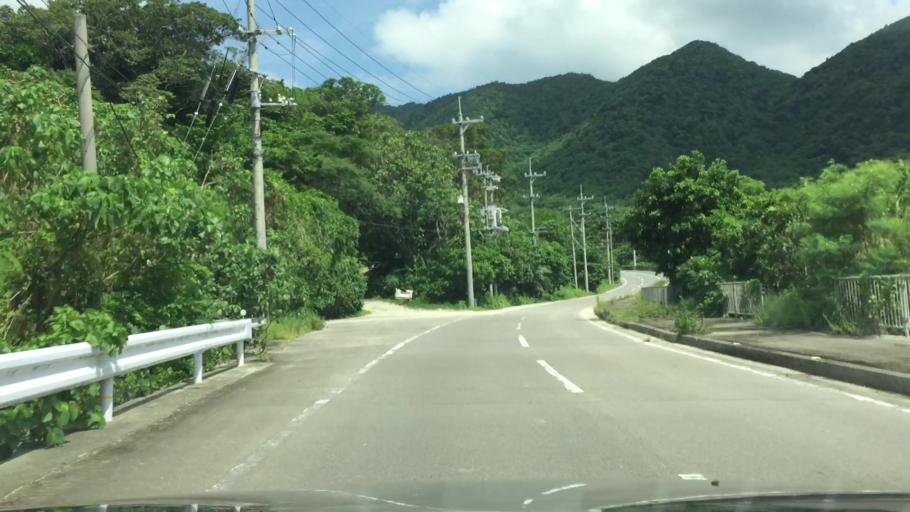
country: JP
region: Okinawa
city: Ishigaki
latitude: 24.4538
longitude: 124.2108
